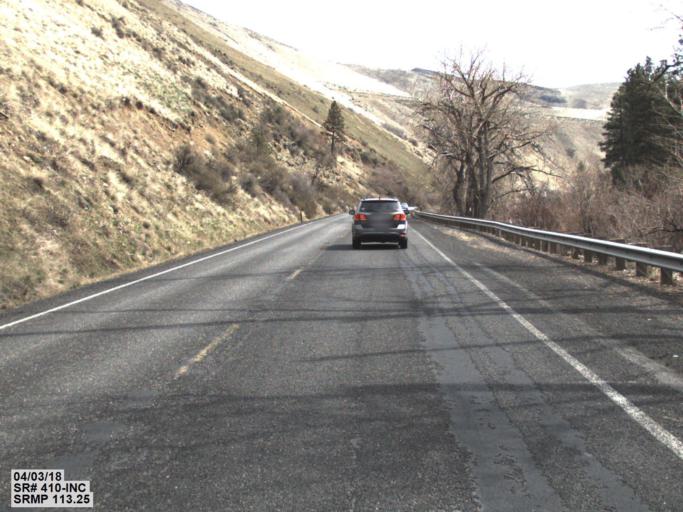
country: US
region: Washington
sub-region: Yakima County
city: Tieton
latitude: 46.7683
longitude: -120.8381
